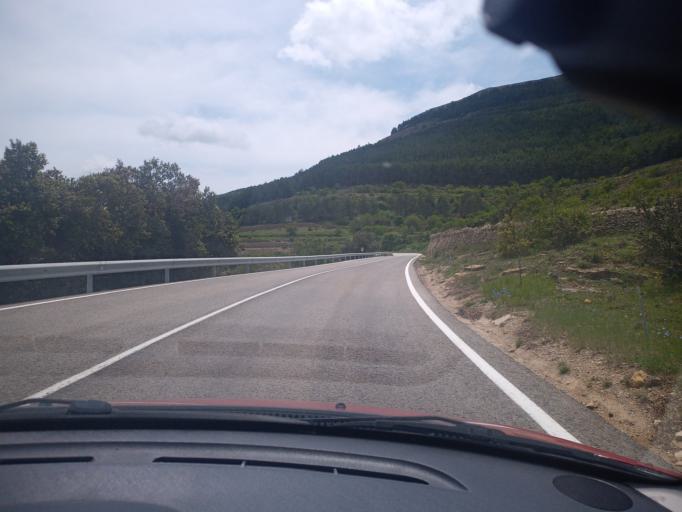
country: ES
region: Valencia
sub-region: Provincia de Castello
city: Ares del Maestre
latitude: 40.4594
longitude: -0.1491
